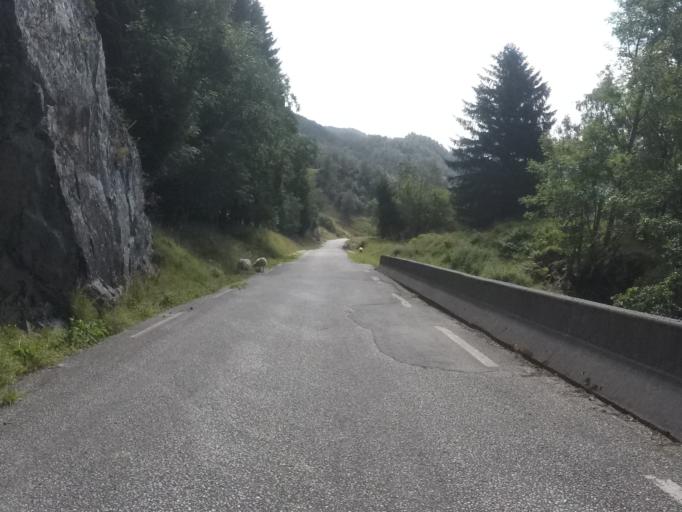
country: NO
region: Hordaland
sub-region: Etne
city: Etne
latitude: 59.7535
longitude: 6.1259
